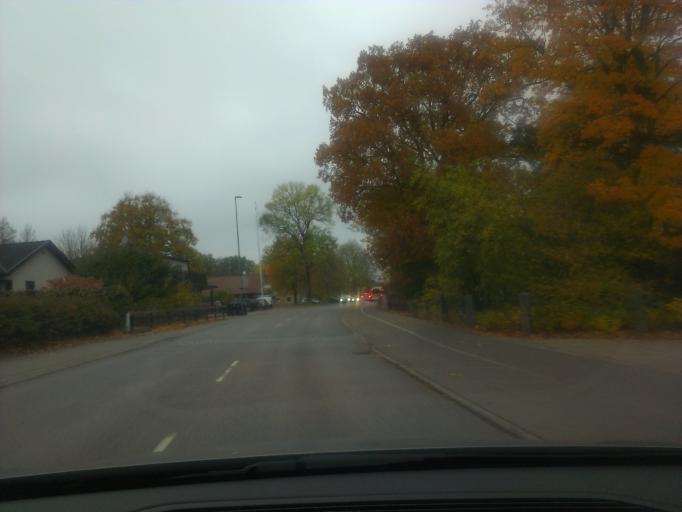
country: SE
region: Kronoberg
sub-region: Vaxjo Kommun
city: Vaexjoe
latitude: 56.9044
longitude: 14.7387
